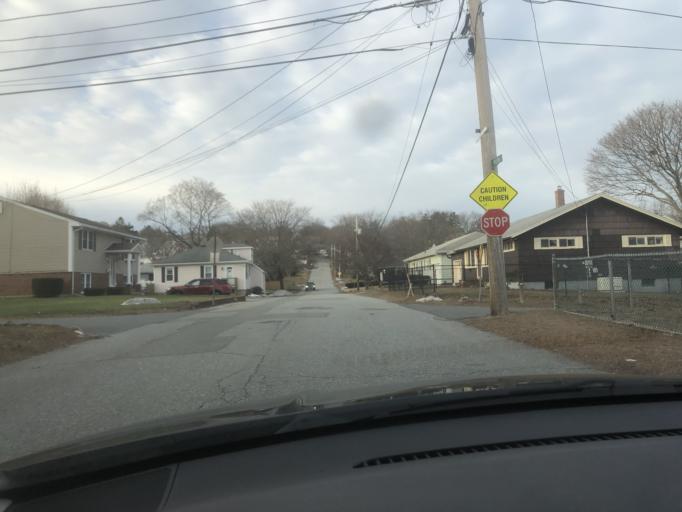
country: US
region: Massachusetts
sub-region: Essex County
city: Lawrence
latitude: 42.7212
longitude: -71.1444
